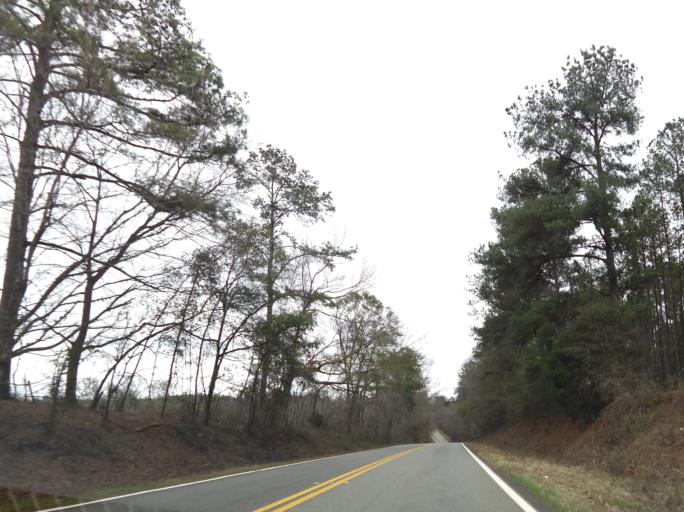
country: US
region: Georgia
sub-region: Twiggs County
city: Jeffersonville
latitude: 32.5640
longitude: -83.3766
